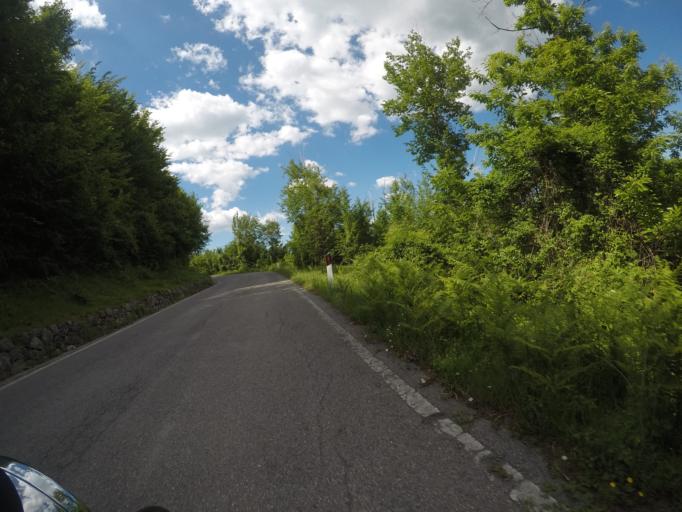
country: IT
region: Tuscany
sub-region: Provincia di Lucca
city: Minucciano
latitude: 44.1683
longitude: 10.2011
